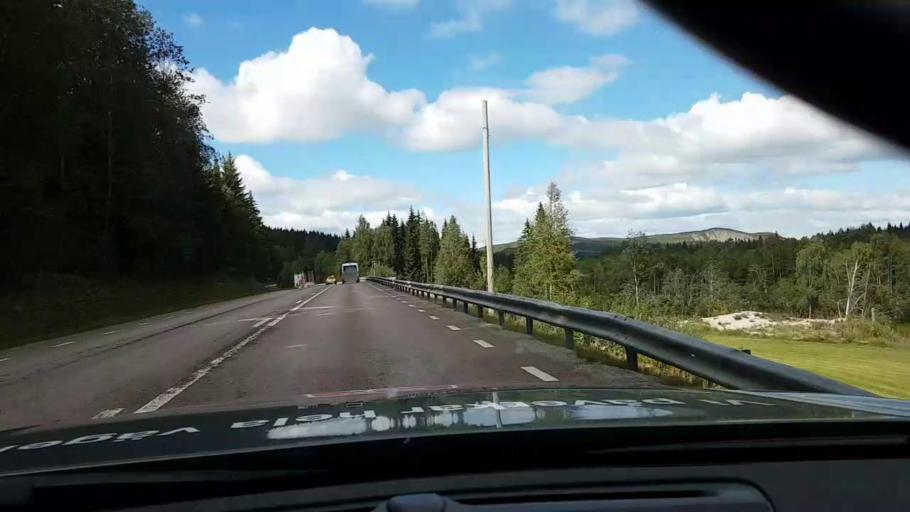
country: SE
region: Vaesternorrland
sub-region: OErnskoeldsviks Kommun
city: Bjasta
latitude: 63.3586
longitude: 18.4747
